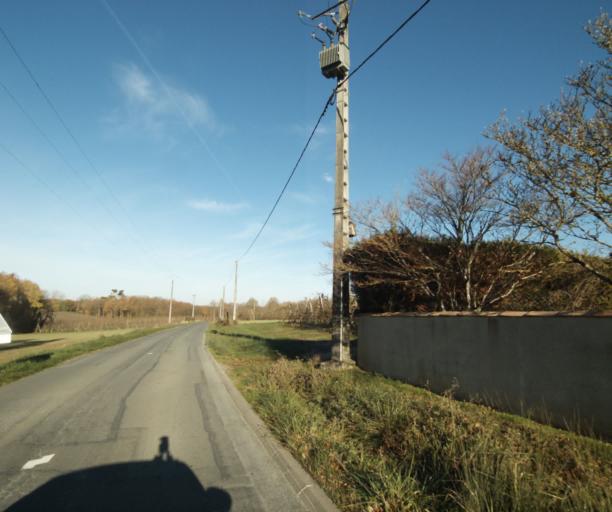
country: FR
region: Poitou-Charentes
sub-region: Departement de la Charente-Maritime
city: Fontcouverte
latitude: 45.7480
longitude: -0.5636
